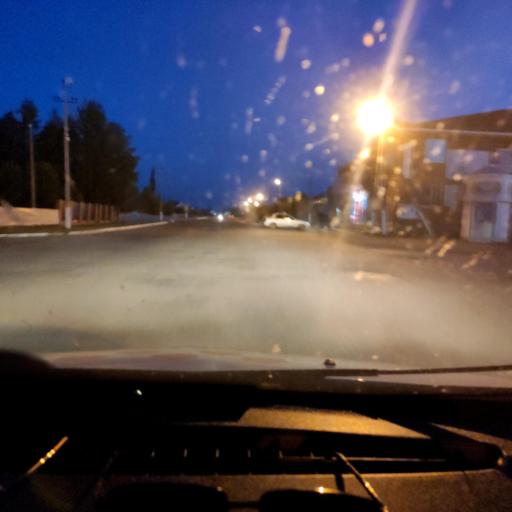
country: RU
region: Bashkortostan
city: Karmaskaly
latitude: 54.3627
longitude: 56.1633
